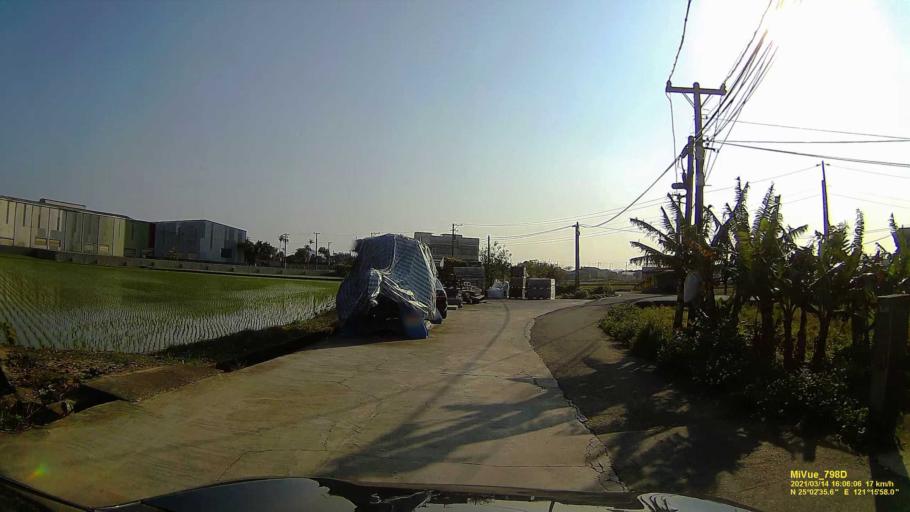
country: TW
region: Taiwan
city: Taoyuan City
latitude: 25.0432
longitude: 121.2660
